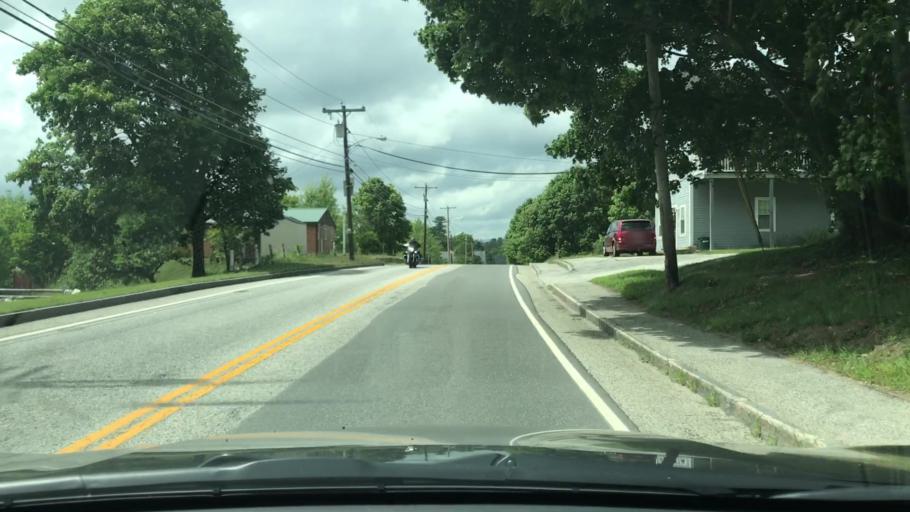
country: US
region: Maine
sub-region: Oxford County
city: Bethel
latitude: 44.3998
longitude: -70.7018
